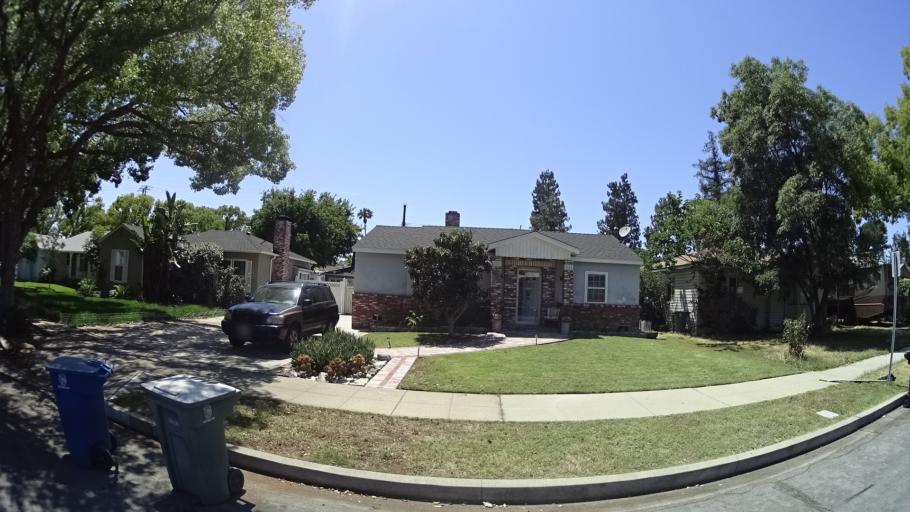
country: US
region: California
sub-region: Los Angeles County
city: North Hollywood
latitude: 34.1785
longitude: -118.3537
